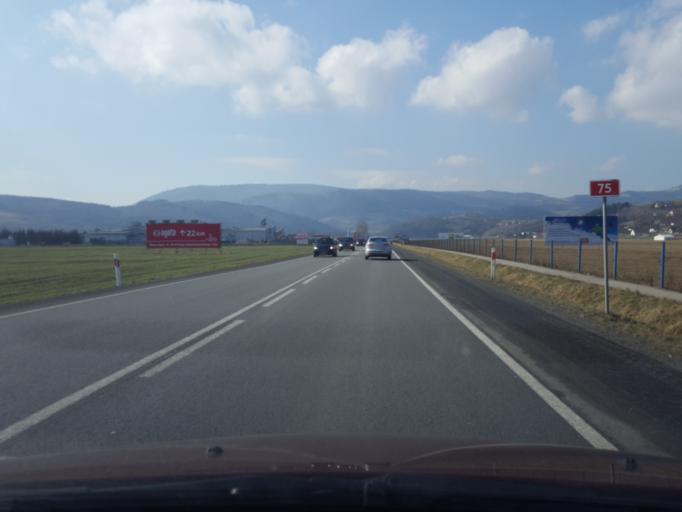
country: PL
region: Lesser Poland Voivodeship
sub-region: Powiat nowosadecki
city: Lososina Dolna
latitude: 49.7485
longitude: 20.6310
